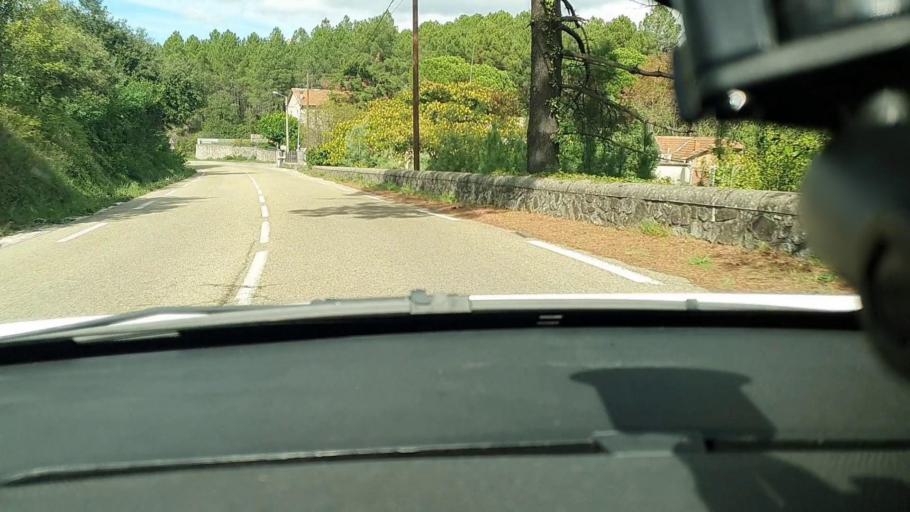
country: FR
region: Languedoc-Roussillon
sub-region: Departement du Gard
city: Laval-Pradel
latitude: 44.2392
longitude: 4.0561
